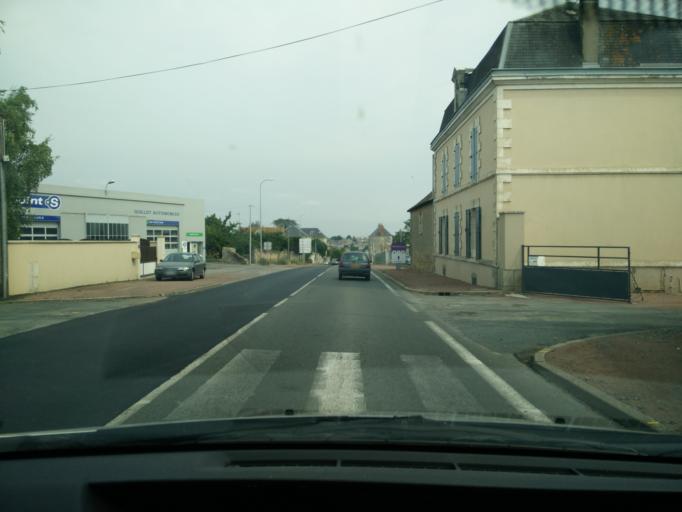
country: FR
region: Poitou-Charentes
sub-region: Departement des Deux-Sevres
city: Saint-Jean-de-Thouars
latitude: 46.9638
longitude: -0.2100
